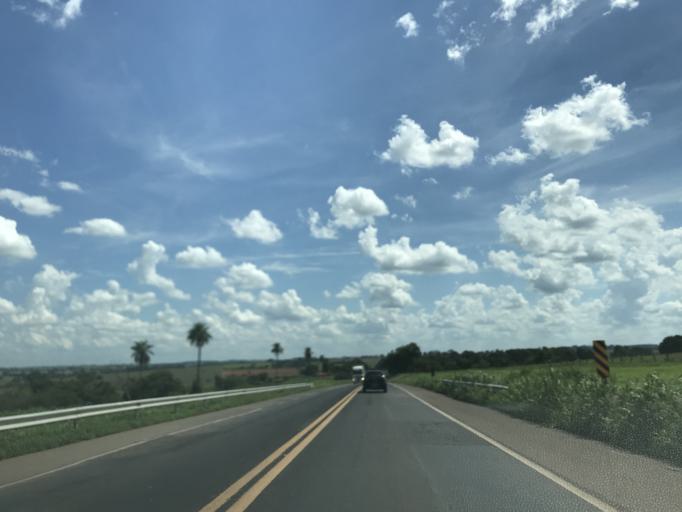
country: BR
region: Sao Paulo
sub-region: Nova Granada
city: Nova Granada
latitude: -20.4630
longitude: -49.2898
